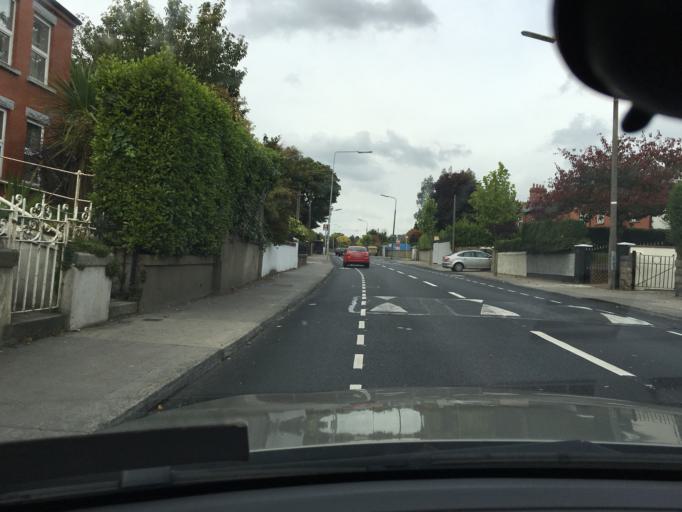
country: IE
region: Leinster
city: Cabra
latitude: 53.3582
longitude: -6.2904
